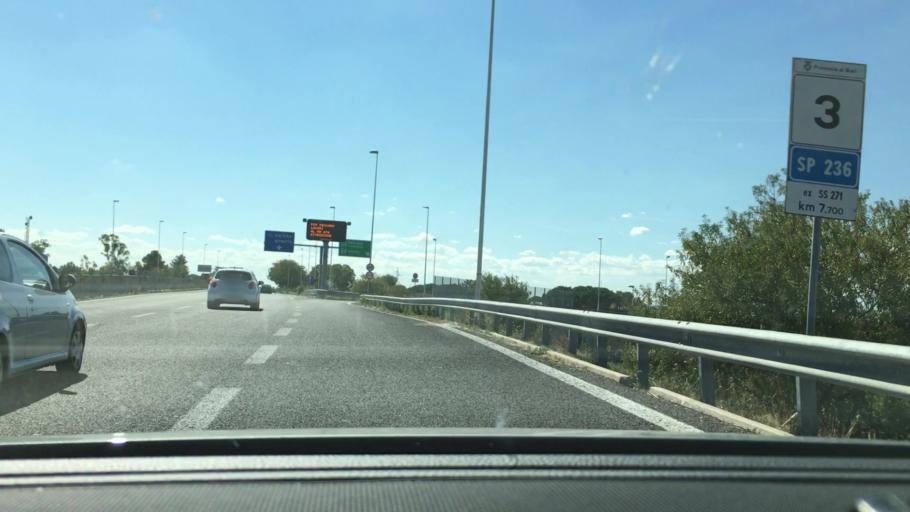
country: IT
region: Apulia
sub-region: Provincia di Bari
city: Bitritto
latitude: 41.0731
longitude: 16.8295
